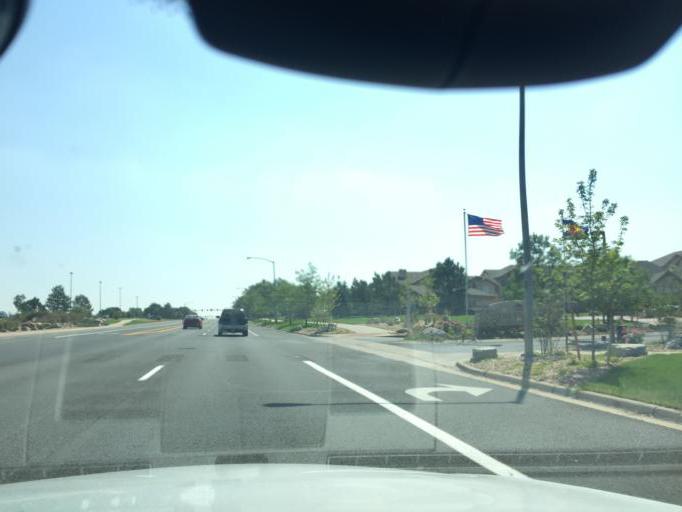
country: US
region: Colorado
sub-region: Broomfield County
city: Broomfield
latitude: 39.8996
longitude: -105.0384
